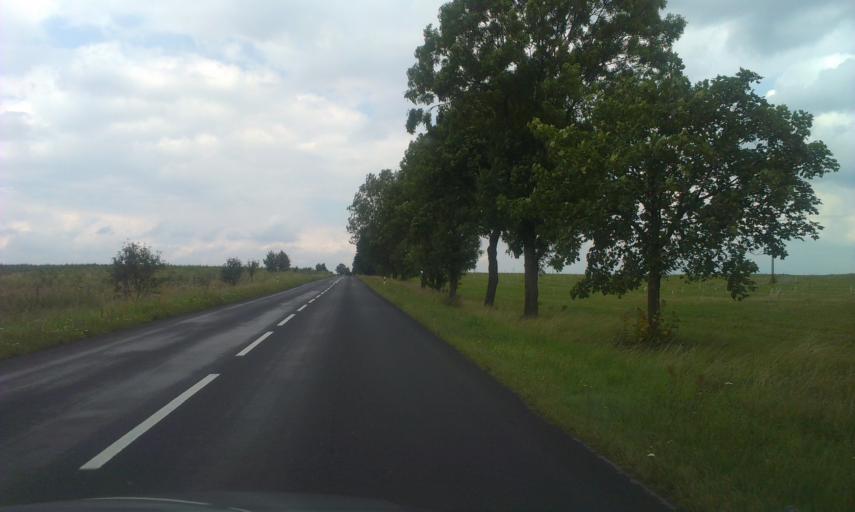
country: PL
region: West Pomeranian Voivodeship
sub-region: Powiat swidwinski
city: Polczyn-Zdroj
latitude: 53.8741
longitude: 16.0695
